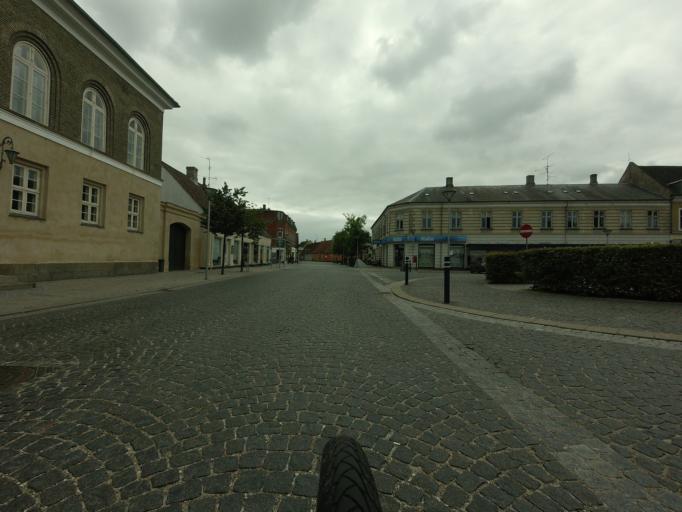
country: DK
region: Zealand
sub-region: Stevns Kommune
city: Store Heddinge
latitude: 55.3097
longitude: 12.3890
